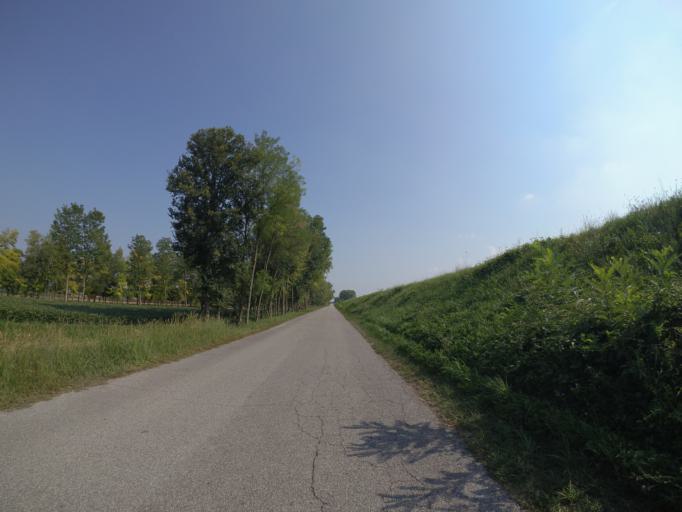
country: IT
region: Friuli Venezia Giulia
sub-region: Provincia di Udine
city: Camino al Tagliamento
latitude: 45.8980
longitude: 12.9440
